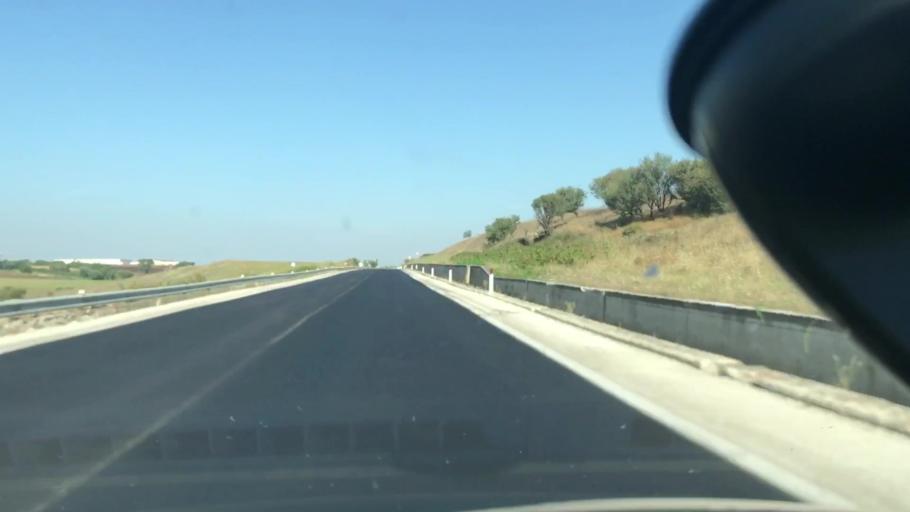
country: IT
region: Apulia
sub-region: Provincia di Barletta - Andria - Trani
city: Spinazzola
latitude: 40.9043
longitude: 16.1139
